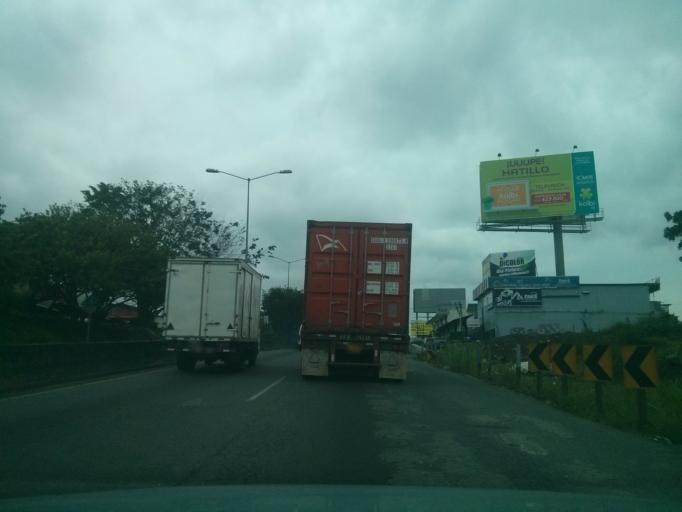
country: CR
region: San Jose
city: San Rafael
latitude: 9.9270
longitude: -84.1147
